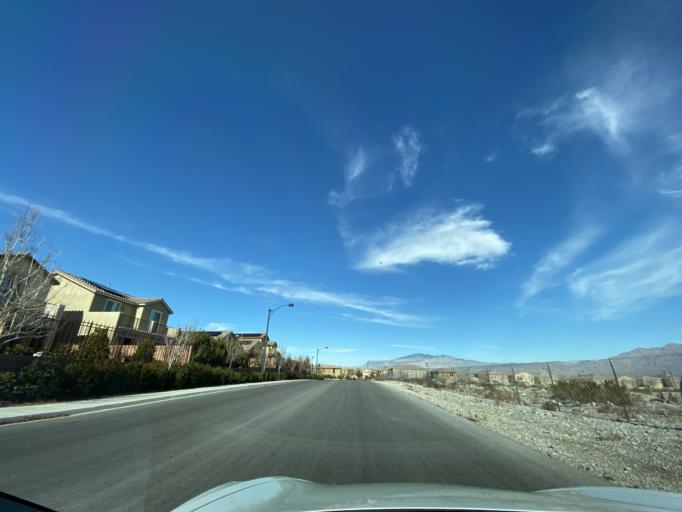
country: US
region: Nevada
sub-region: Clark County
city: Summerlin South
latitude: 36.2980
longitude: -115.3265
